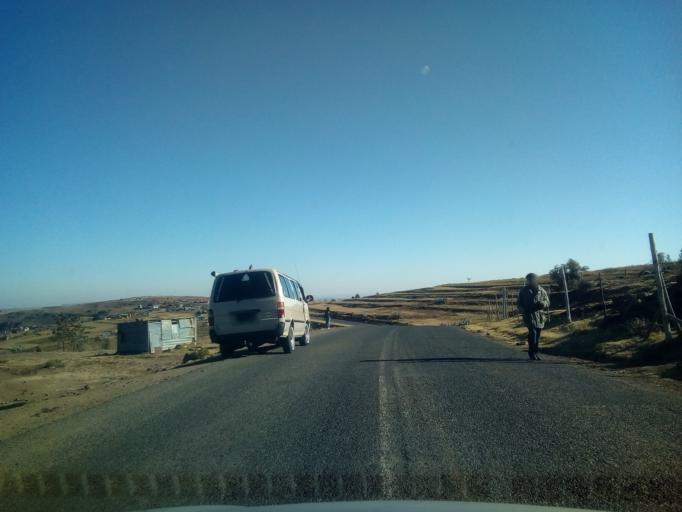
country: LS
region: Berea
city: Teyateyaneng
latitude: -29.2576
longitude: 27.8033
